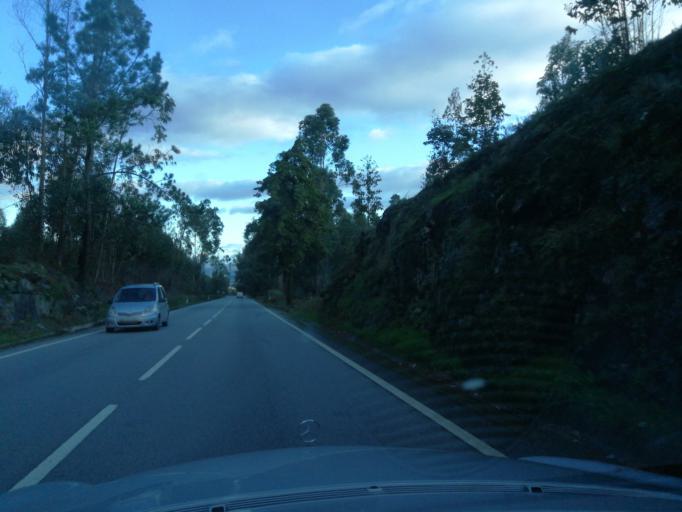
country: PT
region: Braga
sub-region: Barcelos
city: Vila Frescainha
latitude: 41.5676
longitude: -8.6737
